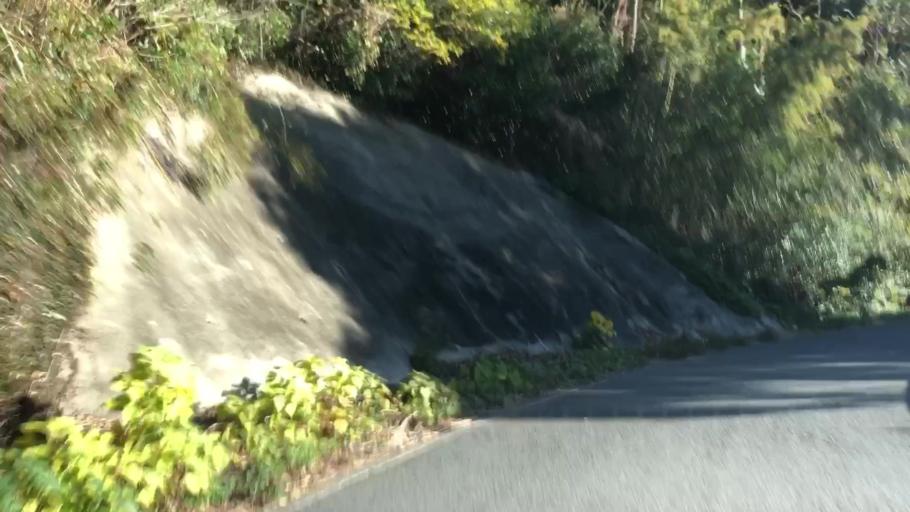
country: JP
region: Nagasaki
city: Sasebo
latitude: 33.0295
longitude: 129.6673
